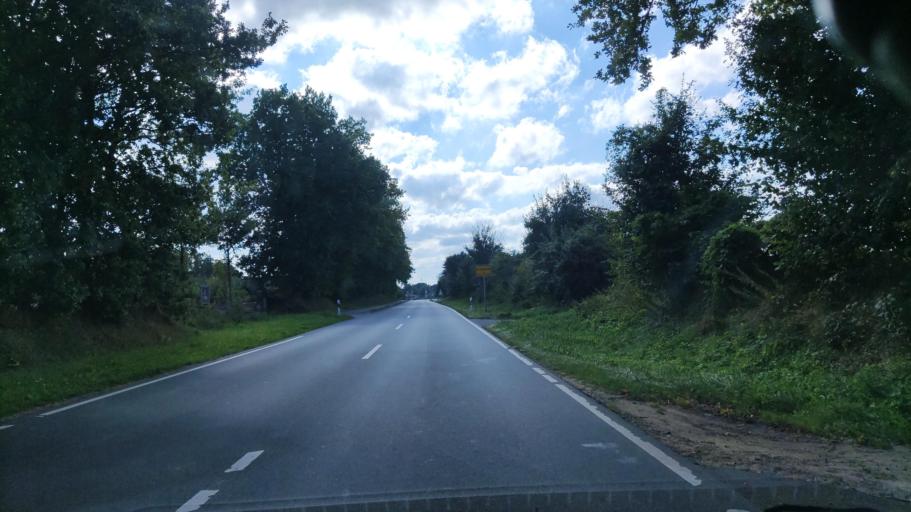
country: DE
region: Schleswig-Holstein
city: Alt Duvenstedt
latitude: 54.3660
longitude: 9.6536
